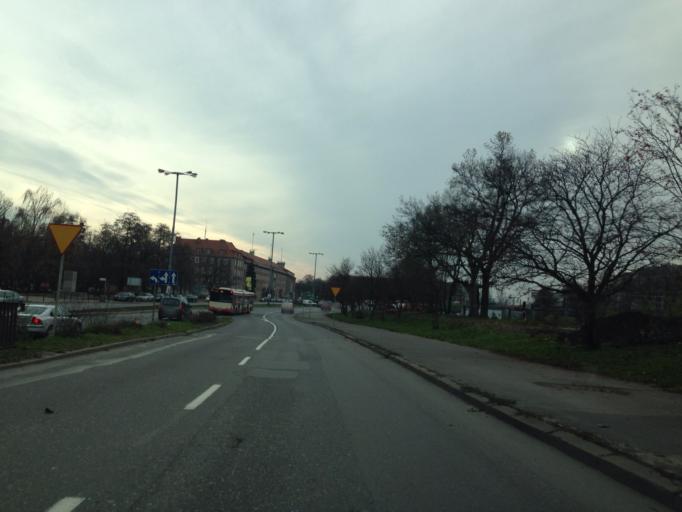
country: PL
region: Pomeranian Voivodeship
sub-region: Gdansk
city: Gdansk
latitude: 54.3470
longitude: 18.6449
